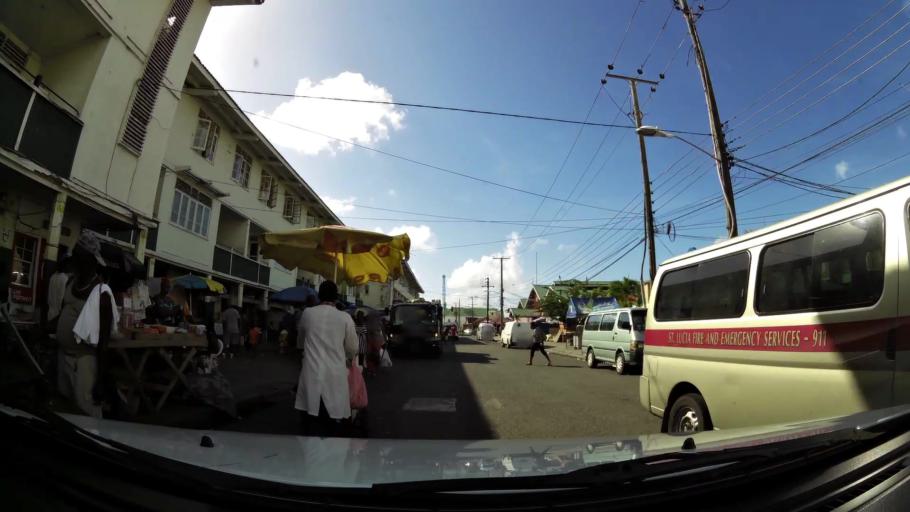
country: LC
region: Castries Quarter
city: Bisee
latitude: 14.0110
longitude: -60.9887
